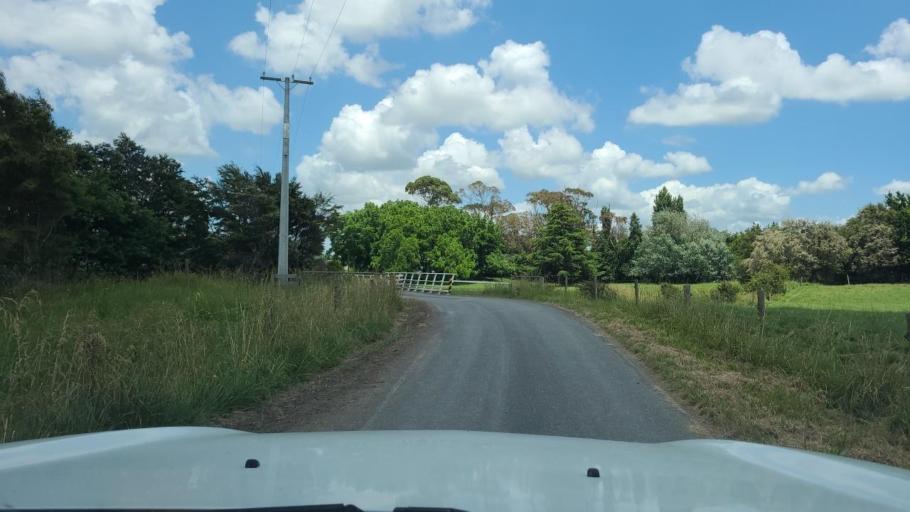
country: NZ
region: Waikato
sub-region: Hauraki District
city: Ngatea
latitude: -37.5114
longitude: 175.4404
